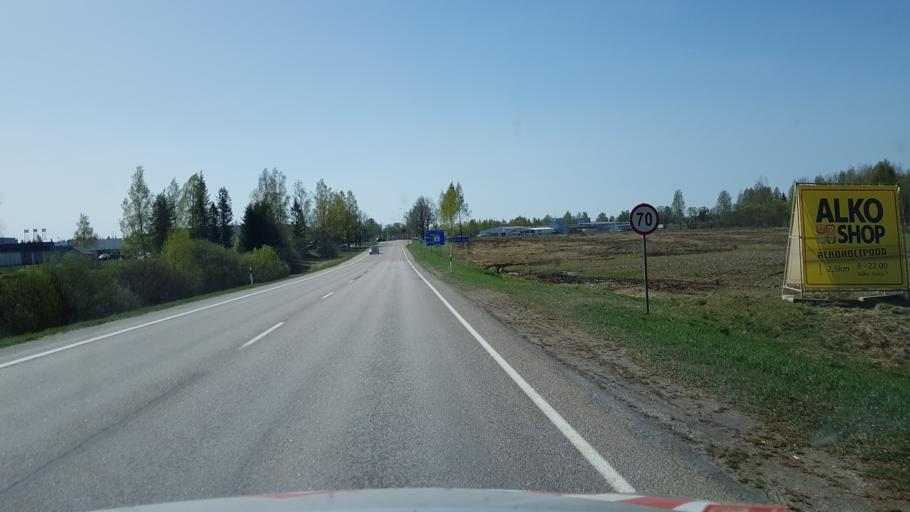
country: EE
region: Valgamaa
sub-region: Valga linn
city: Valga
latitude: 57.7952
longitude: 26.0344
